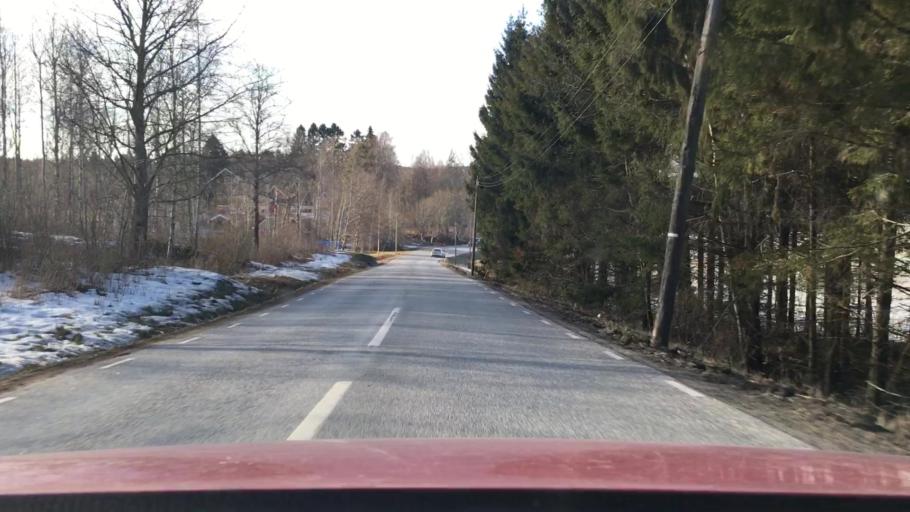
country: SE
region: Vaestra Goetaland
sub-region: Tanums Kommun
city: Tanumshede
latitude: 58.8113
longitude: 11.5486
